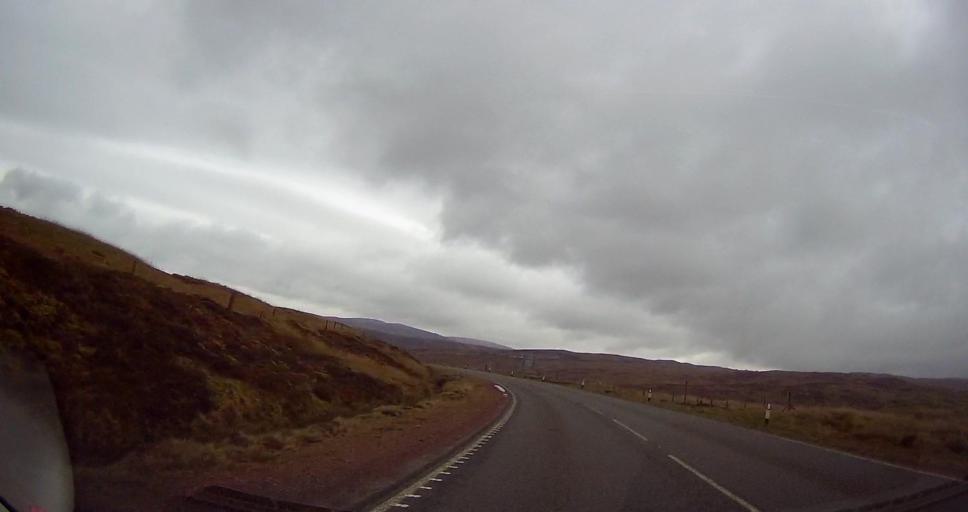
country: GB
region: Scotland
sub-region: Shetland Islands
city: Lerwick
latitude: 60.2649
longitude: -1.2225
